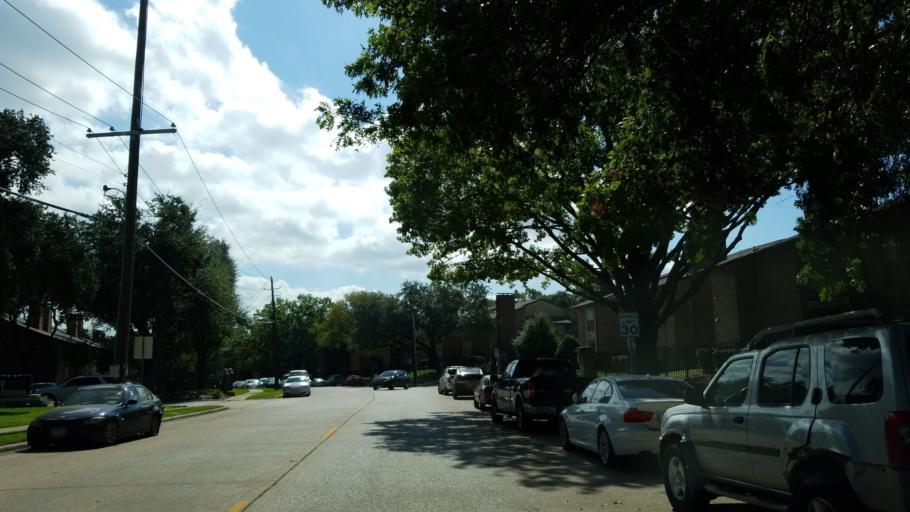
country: US
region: Texas
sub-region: Dallas County
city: Addison
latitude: 32.9428
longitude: -96.8091
